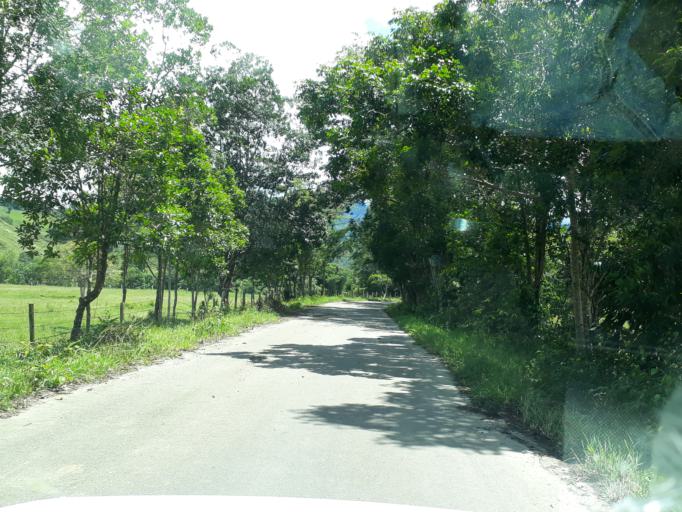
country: CO
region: Cundinamarca
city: Medina
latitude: 4.5785
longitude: -73.3297
